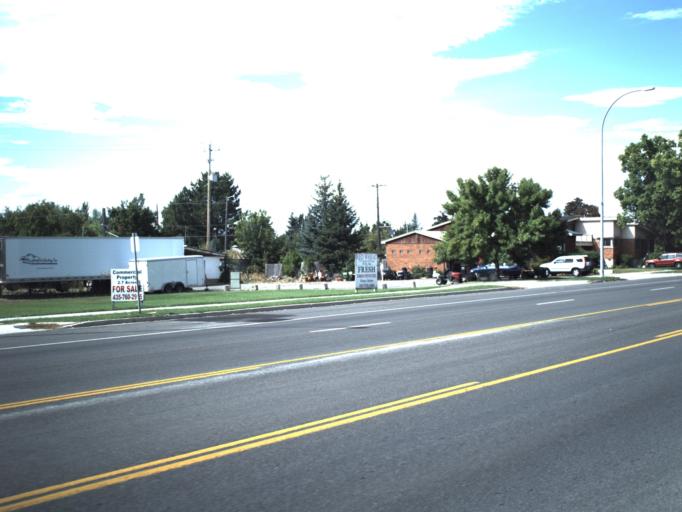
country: US
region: Utah
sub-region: Cache County
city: Smithfield
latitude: 41.8457
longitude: -111.8324
